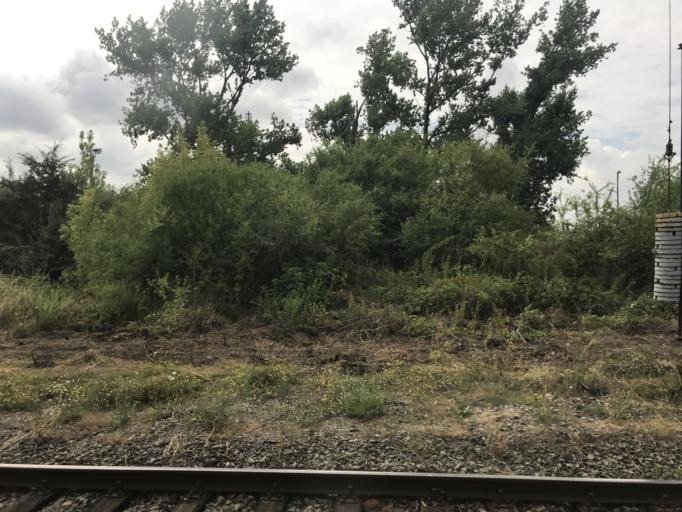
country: PL
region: Greater Poland Voivodeship
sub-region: Powiat gnieznienski
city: Gniezno
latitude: 52.5313
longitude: 17.6230
